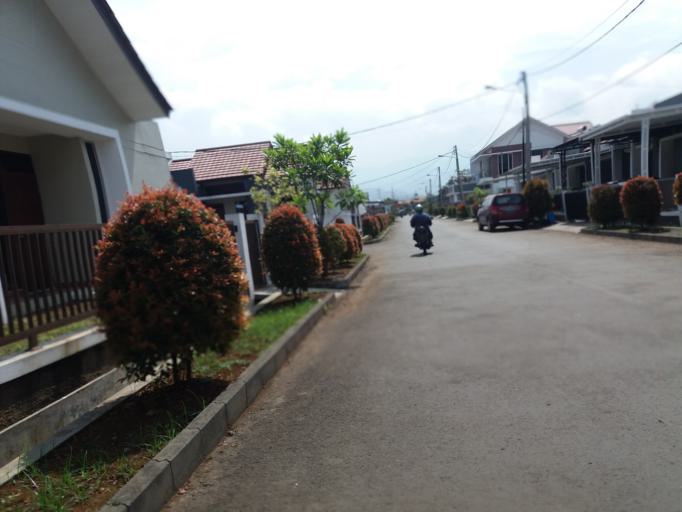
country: ID
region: West Java
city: Bandung
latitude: -6.9238
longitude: 107.6679
